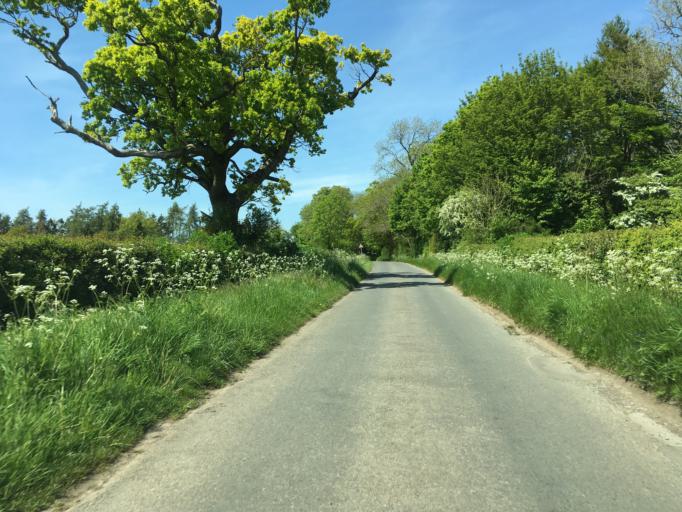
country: GB
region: England
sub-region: Gloucestershire
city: Coates
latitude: 51.6834
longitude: -1.9990
